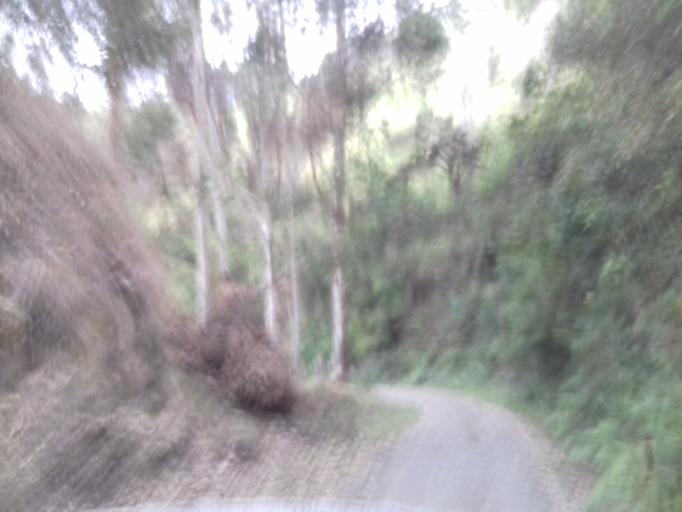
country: CO
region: Tolima
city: Cajamarca
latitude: 4.5351
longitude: -75.4687
